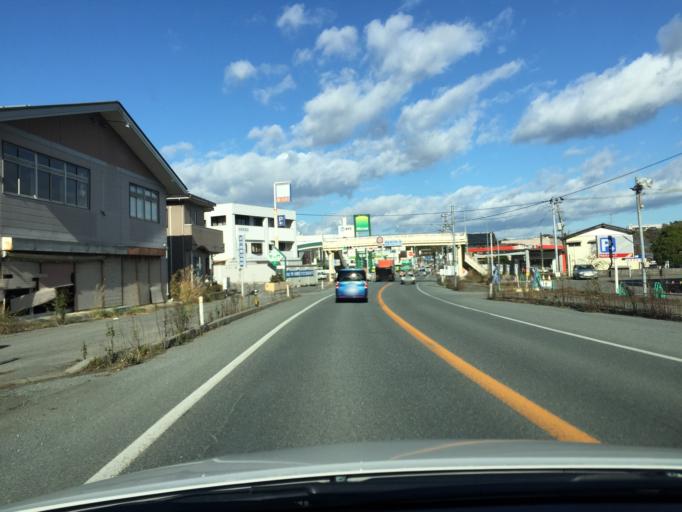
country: JP
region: Fukushima
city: Namie
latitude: 37.3364
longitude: 141.0147
